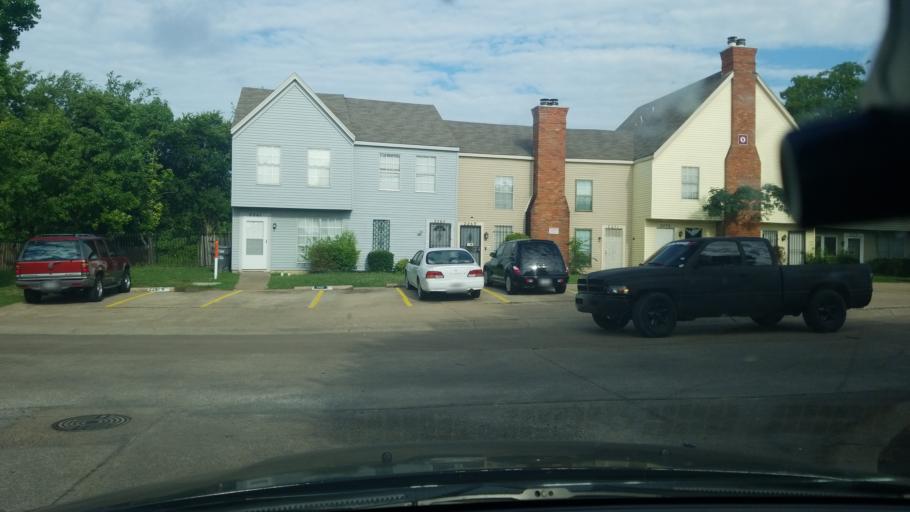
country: US
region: Texas
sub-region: Dallas County
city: Balch Springs
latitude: 32.7515
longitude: -96.6600
